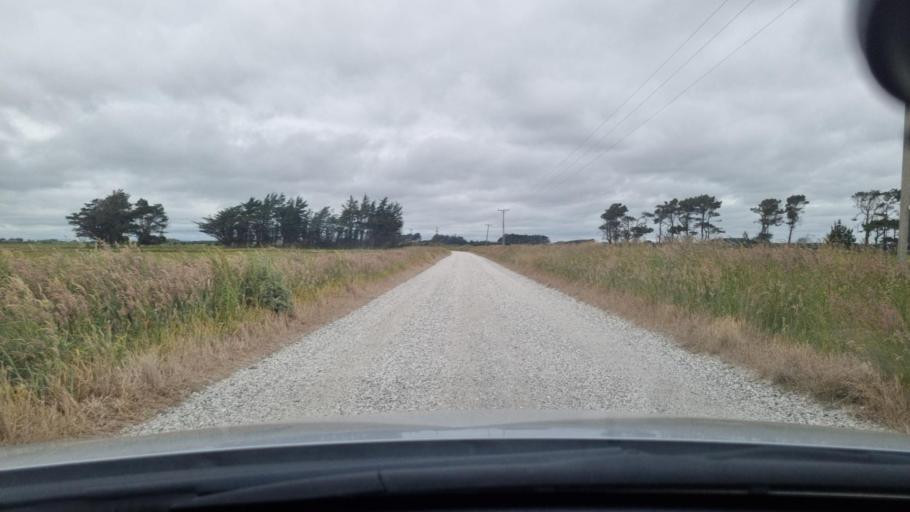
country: NZ
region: Southland
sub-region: Invercargill City
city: Invercargill
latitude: -46.3881
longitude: 168.2792
